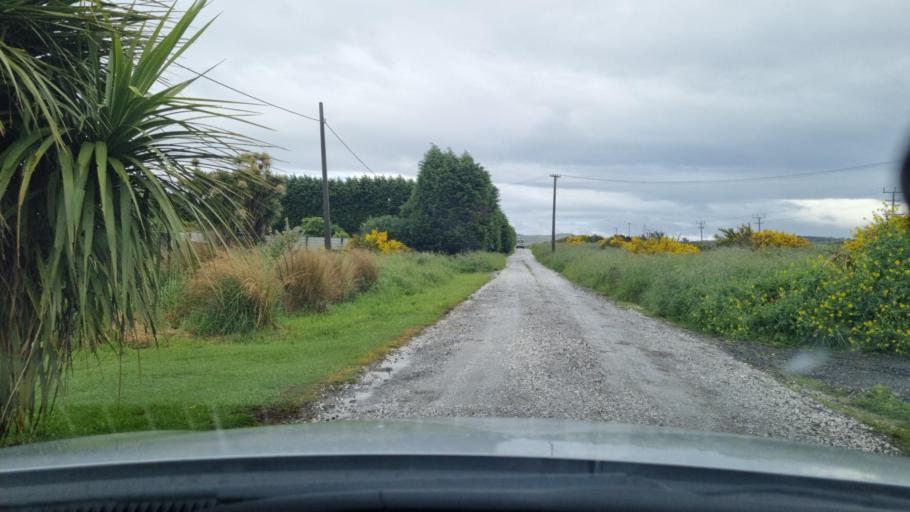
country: NZ
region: Southland
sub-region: Invercargill City
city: Bluff
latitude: -46.5417
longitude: 168.3024
